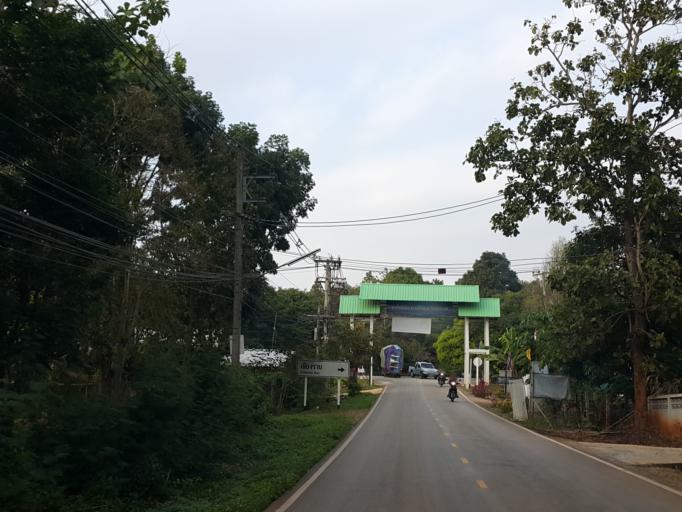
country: TH
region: Chiang Mai
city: Mae On
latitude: 18.9172
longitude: 99.2357
